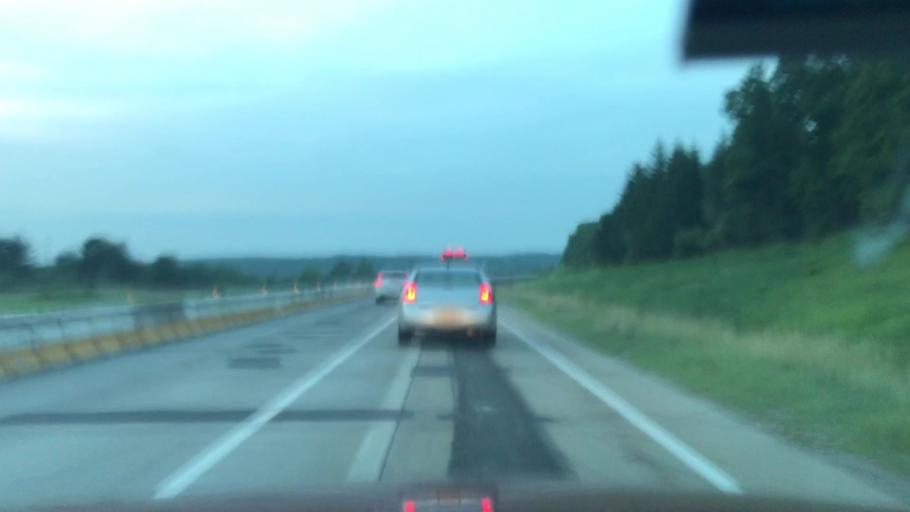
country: US
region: Michigan
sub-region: Kent County
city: Rockford
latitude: 43.1424
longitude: -85.5891
